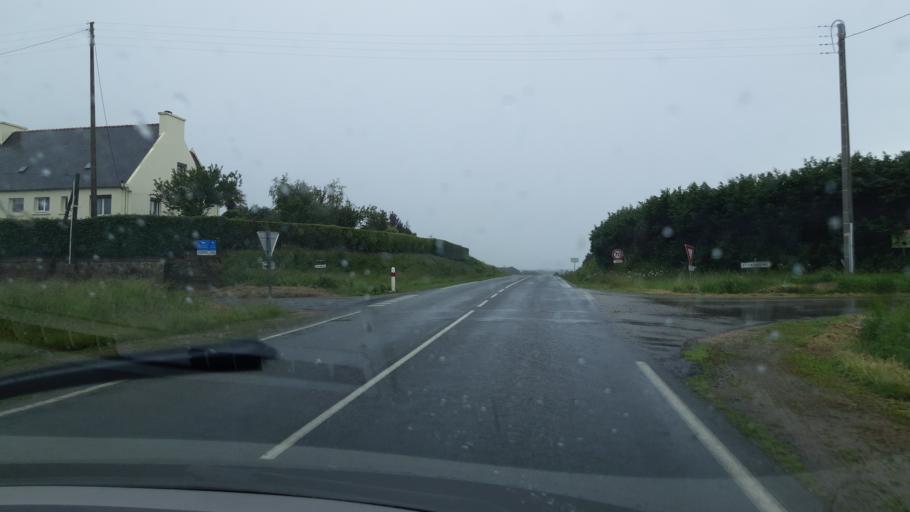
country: FR
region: Brittany
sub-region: Departement du Finistere
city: Plougoulm
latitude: 48.6227
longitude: -4.0555
